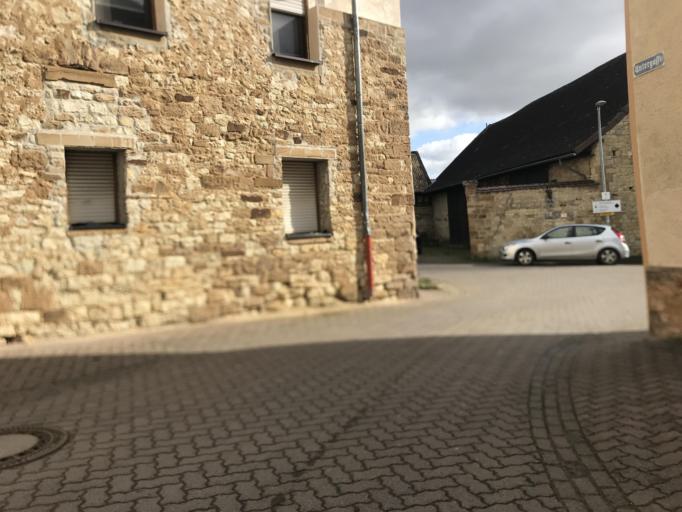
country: DE
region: Rheinland-Pfalz
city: Sankt Johann
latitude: 49.8660
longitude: 8.0169
